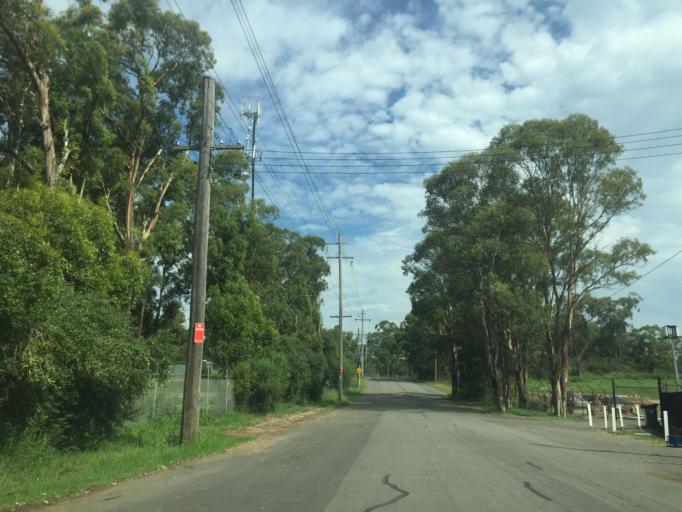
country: AU
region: New South Wales
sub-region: Holroyd
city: Girraween
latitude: -33.8074
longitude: 150.9138
